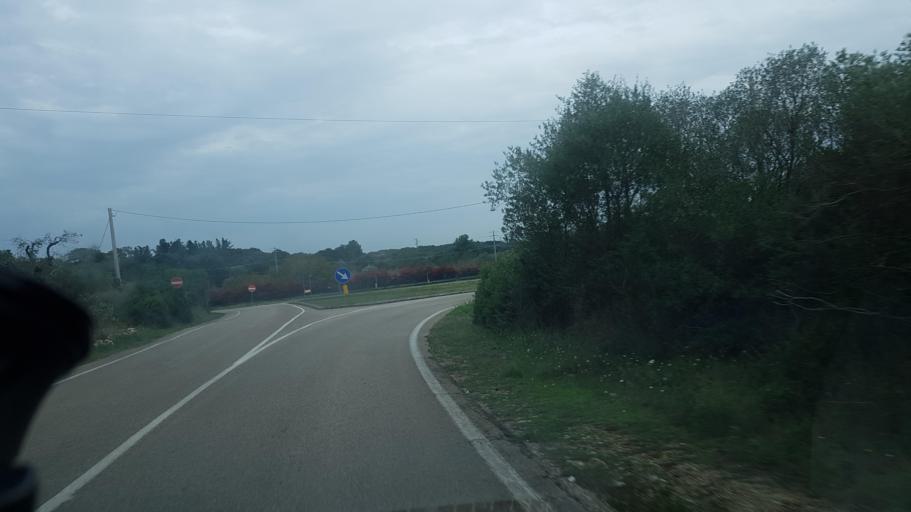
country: IT
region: Apulia
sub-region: Provincia di Brindisi
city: Ostuni
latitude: 40.7365
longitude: 17.5416
